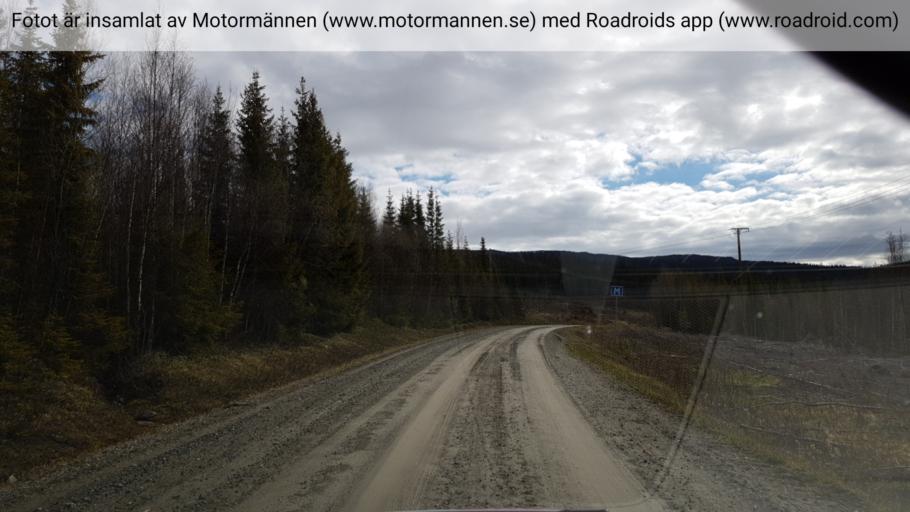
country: SE
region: Vaesterbotten
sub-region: Vilhelmina Kommun
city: Sjoberg
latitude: 65.5633
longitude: 15.3780
